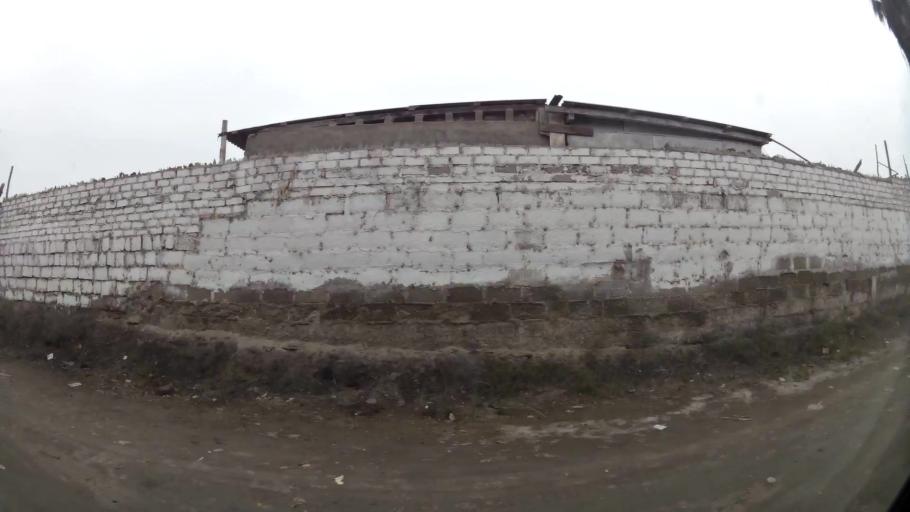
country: PE
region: Lima
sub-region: Lima
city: Surco
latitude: -12.2036
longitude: -76.9852
